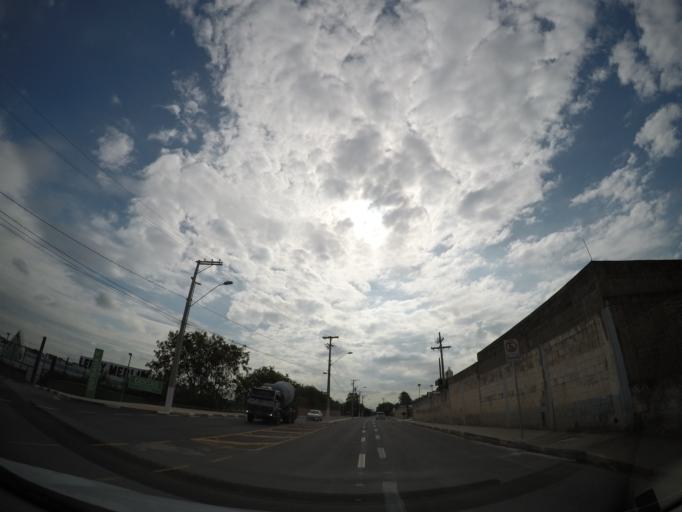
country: BR
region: Sao Paulo
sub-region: Campinas
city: Campinas
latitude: -22.9032
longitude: -47.1093
